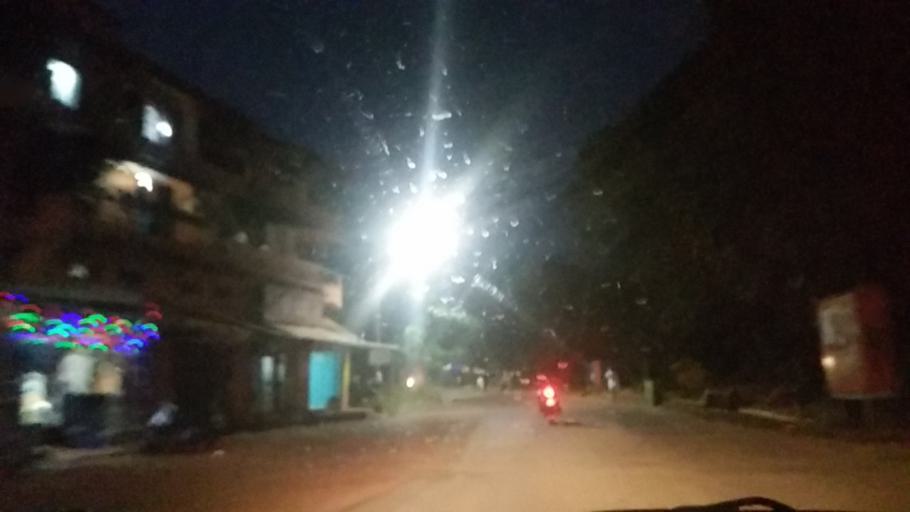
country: IN
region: Goa
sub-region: South Goa
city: Raia
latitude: 15.2983
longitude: 73.9604
